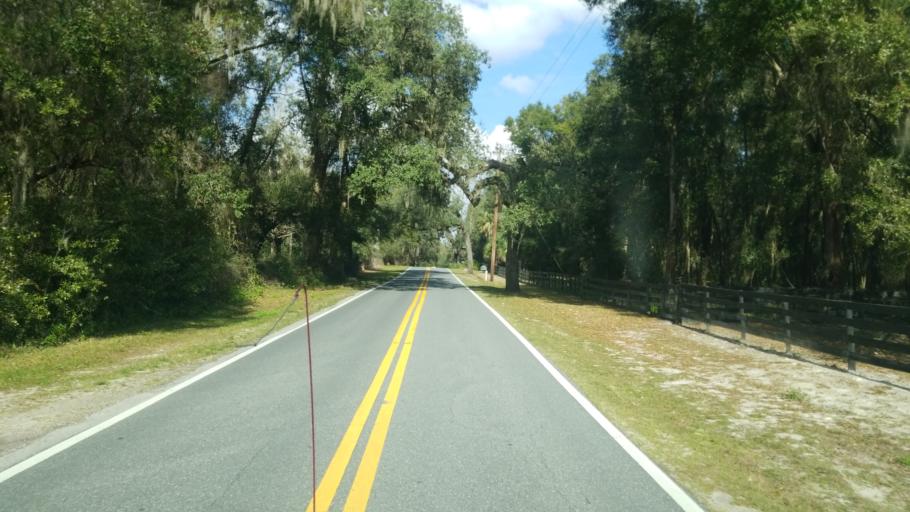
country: US
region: Florida
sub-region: Citrus County
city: Floral City
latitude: 28.7412
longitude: -82.2638
